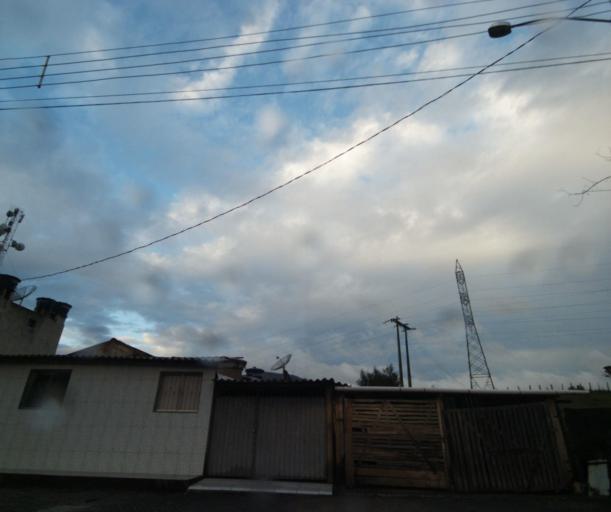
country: BR
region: Espirito Santo
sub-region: Muniz Freire
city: Muniz Freire
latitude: -20.4690
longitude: -41.4128
